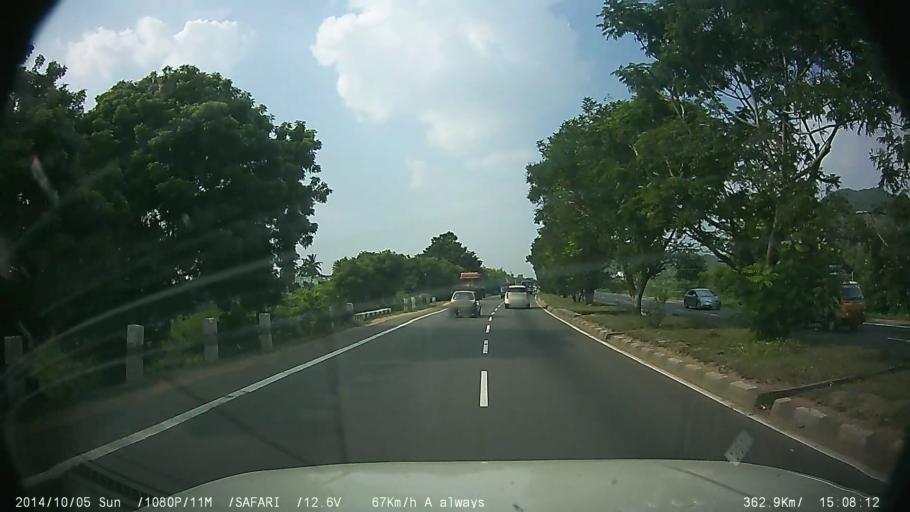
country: IN
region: Tamil Nadu
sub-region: Kancheepuram
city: Chengalpattu
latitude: 12.6674
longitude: 79.9588
